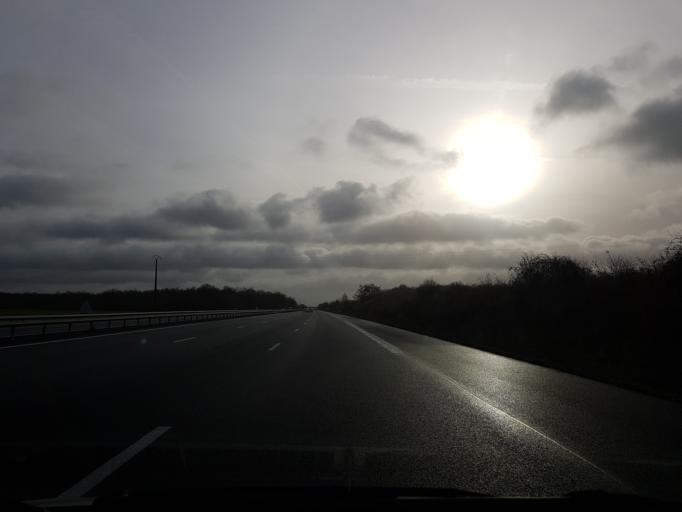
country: FR
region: Ile-de-France
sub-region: Departement de Seine-et-Marne
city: Le Chatelet-en-Brie
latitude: 48.4893
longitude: 2.8483
